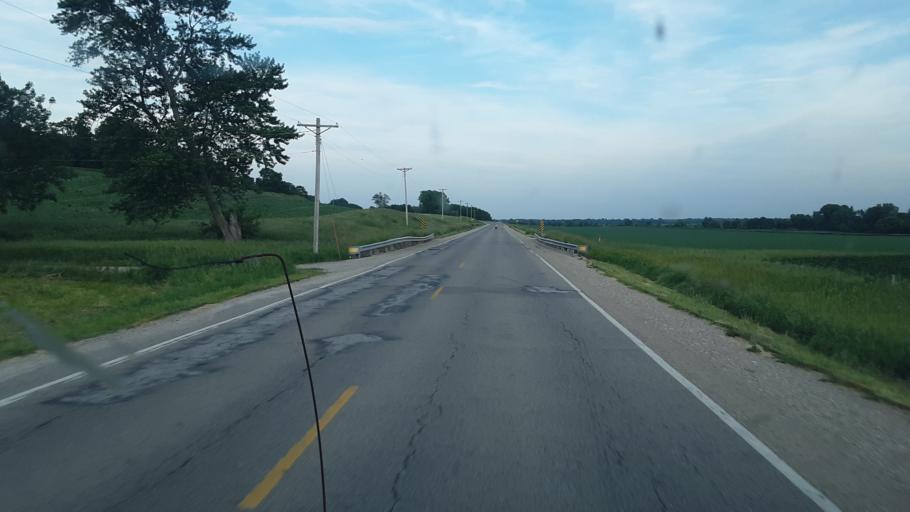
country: US
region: Iowa
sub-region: Benton County
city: Belle Plaine
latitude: 41.9085
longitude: -92.3387
